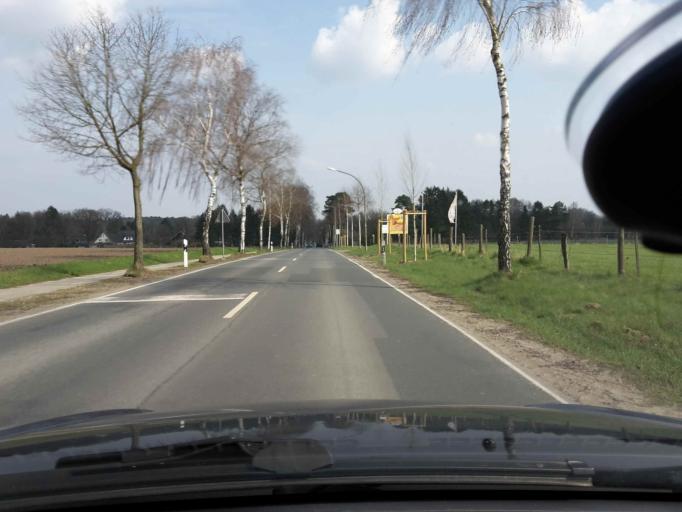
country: DE
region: Lower Saxony
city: Buchholz in der Nordheide
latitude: 53.2970
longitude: 9.8709
